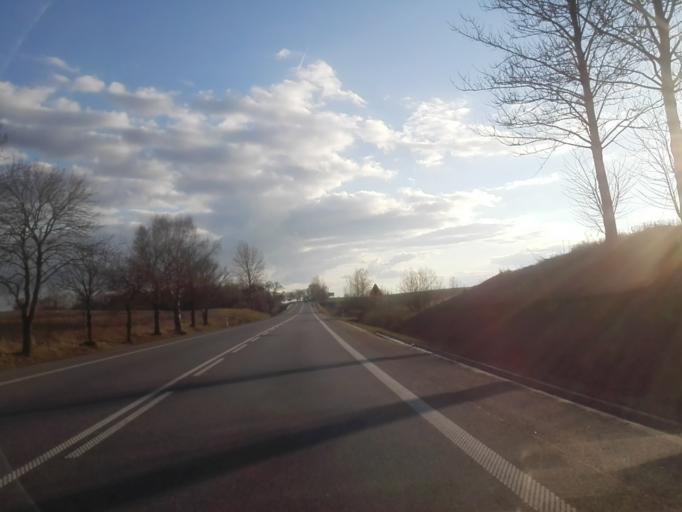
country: PL
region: Podlasie
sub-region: Suwalki
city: Suwalki
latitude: 54.1907
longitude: 23.0098
